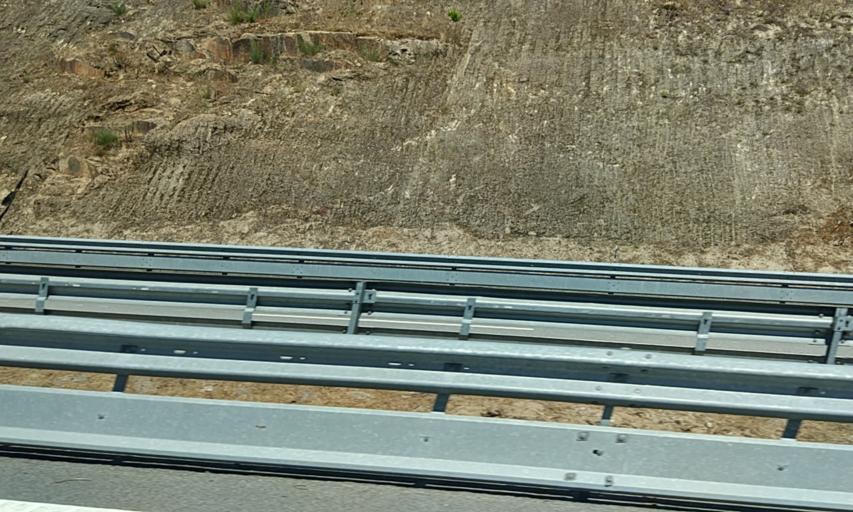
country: PT
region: Porto
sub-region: Amarante
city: Amarante
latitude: 41.2603
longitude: -8.0326
